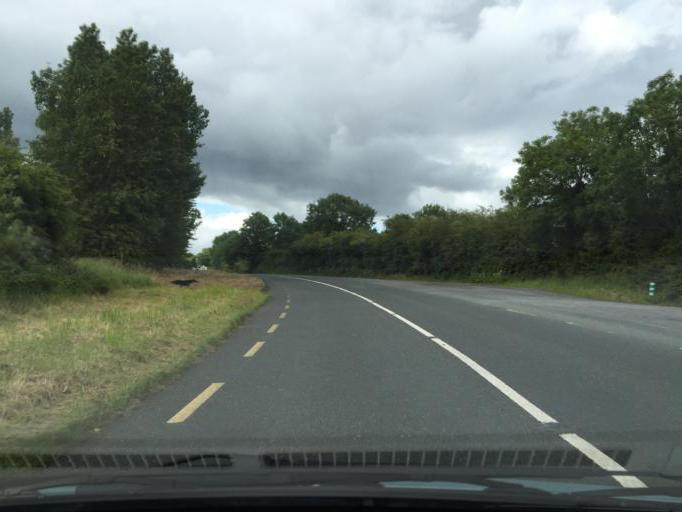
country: IE
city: Ballisodare
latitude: 54.2324
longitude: -8.4843
